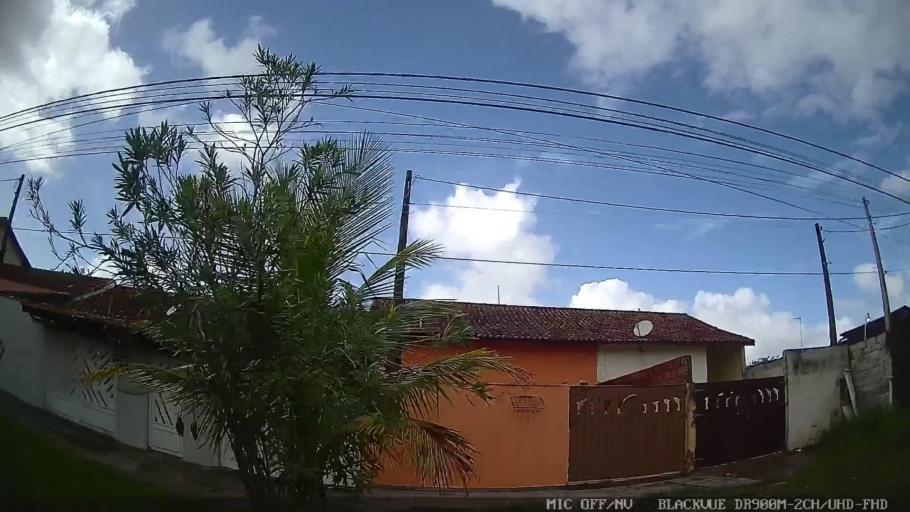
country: BR
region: Sao Paulo
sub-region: Itanhaem
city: Itanhaem
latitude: -24.2069
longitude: -46.8410
